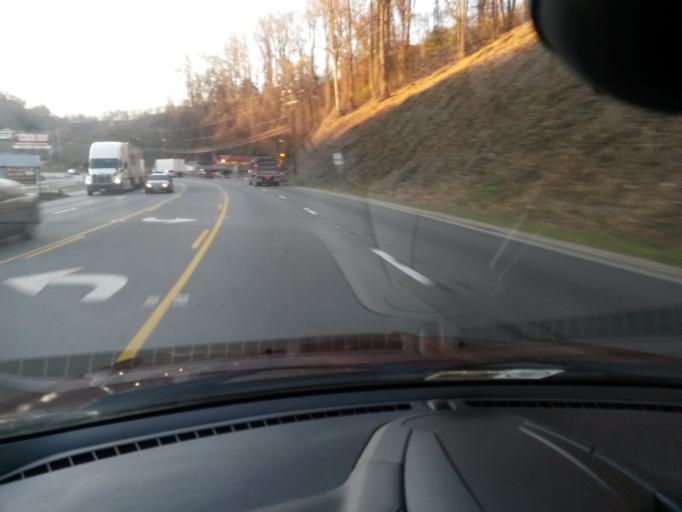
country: US
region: Virginia
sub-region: Roanoke County
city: Narrows
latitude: 37.1166
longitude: -79.9566
